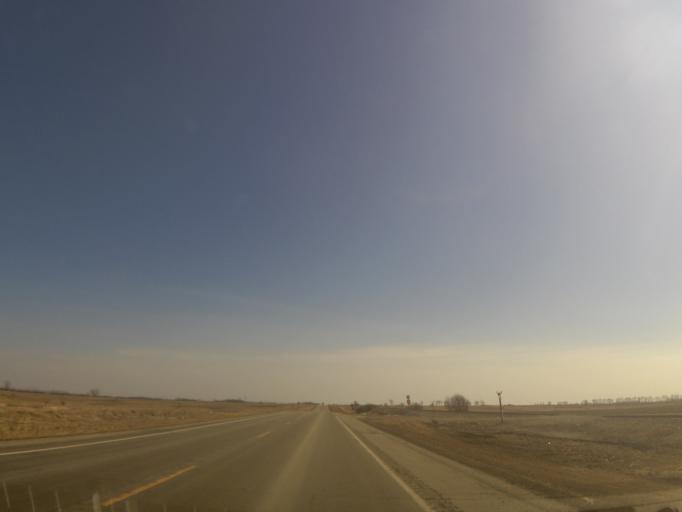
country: US
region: North Dakota
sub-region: Walsh County
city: Grafton
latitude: 48.1953
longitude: -97.3295
